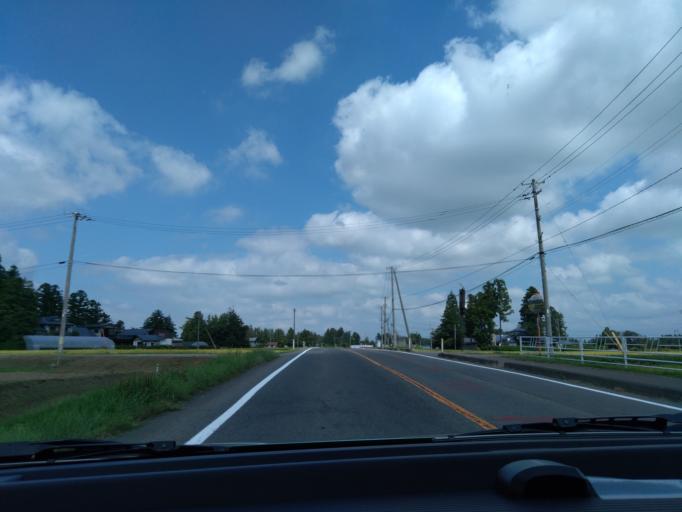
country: JP
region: Iwate
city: Hanamaki
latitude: 39.4271
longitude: 141.0894
